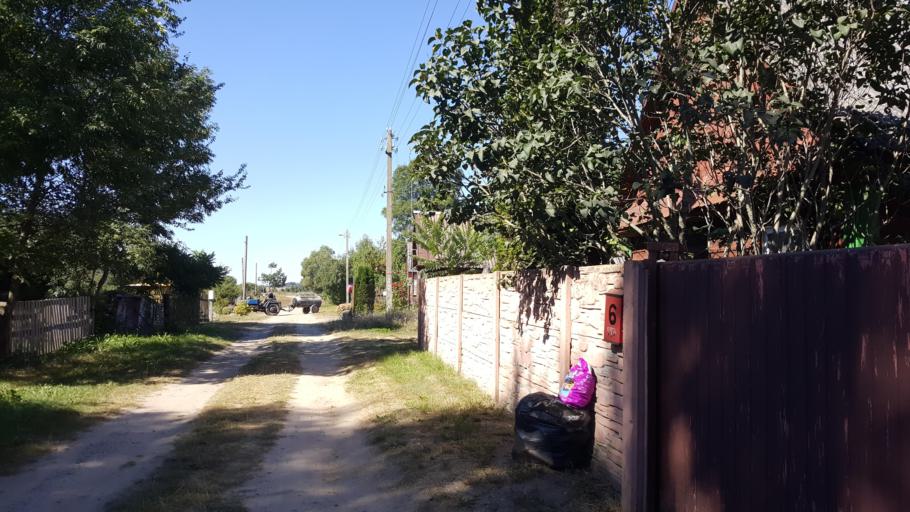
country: PL
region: Lublin Voivodeship
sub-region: Powiat bialski
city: Terespol
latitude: 52.2107
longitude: 23.5231
